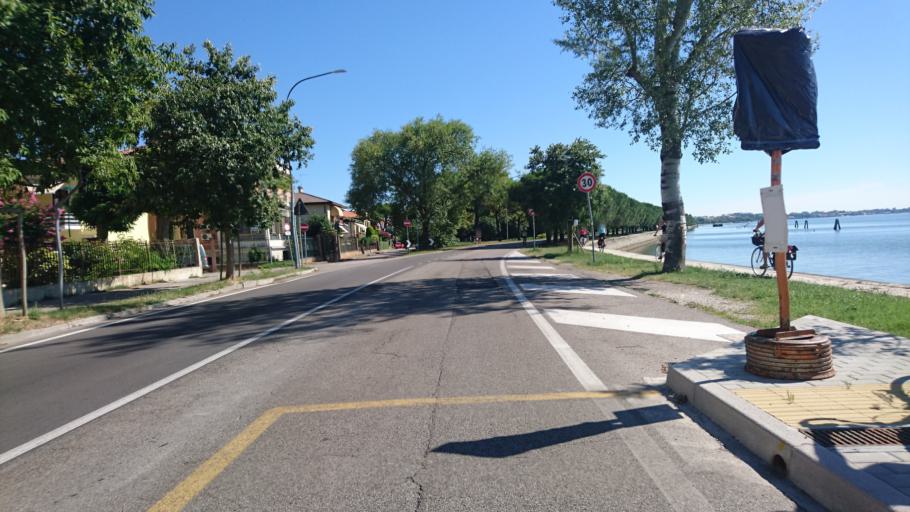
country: IT
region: Veneto
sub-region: Provincia di Venezia
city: Lido
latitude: 45.3697
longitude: 12.3369
